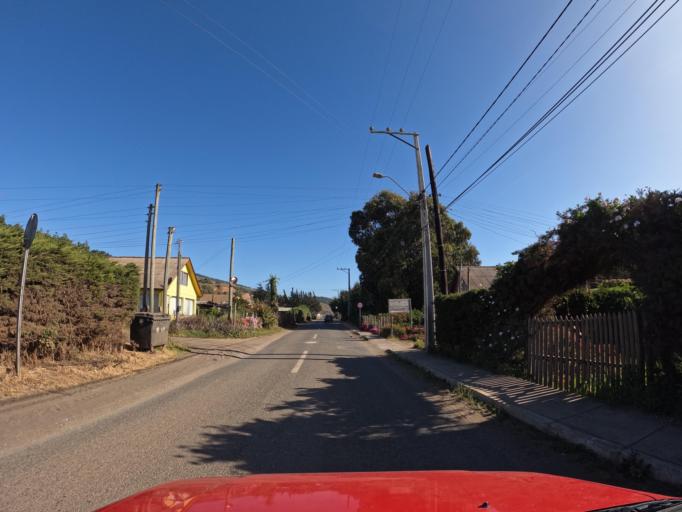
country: CL
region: Maule
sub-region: Provincia de Talca
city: Constitucion
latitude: -34.8478
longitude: -72.1413
